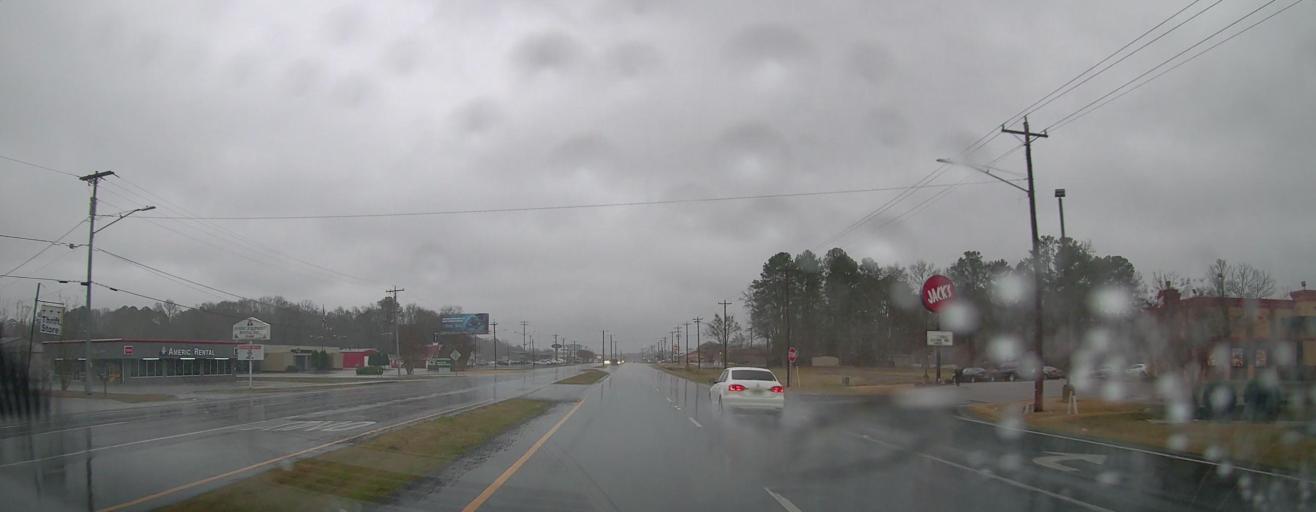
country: US
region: Alabama
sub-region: Morgan County
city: Hartselle
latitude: 34.4517
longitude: -86.9462
